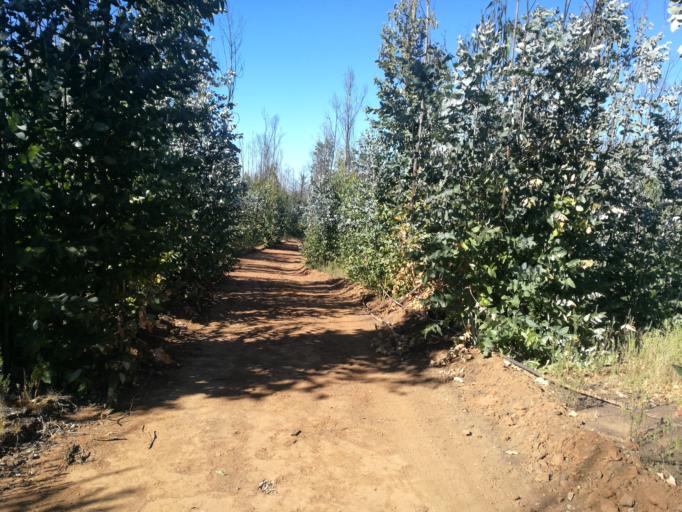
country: CL
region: Valparaiso
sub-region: Provincia de Valparaiso
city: Valparaiso
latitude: -33.0699
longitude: -71.6487
